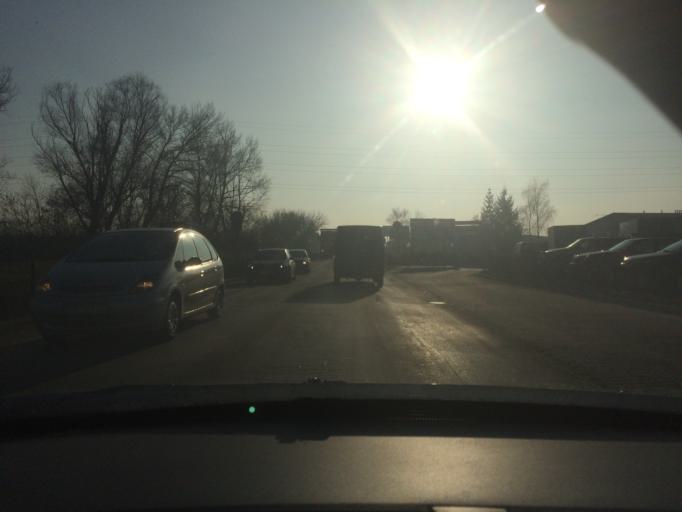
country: PL
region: Lesser Poland Voivodeship
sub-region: Powiat wielicki
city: Czarnochowice
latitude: 50.0353
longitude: 20.0423
